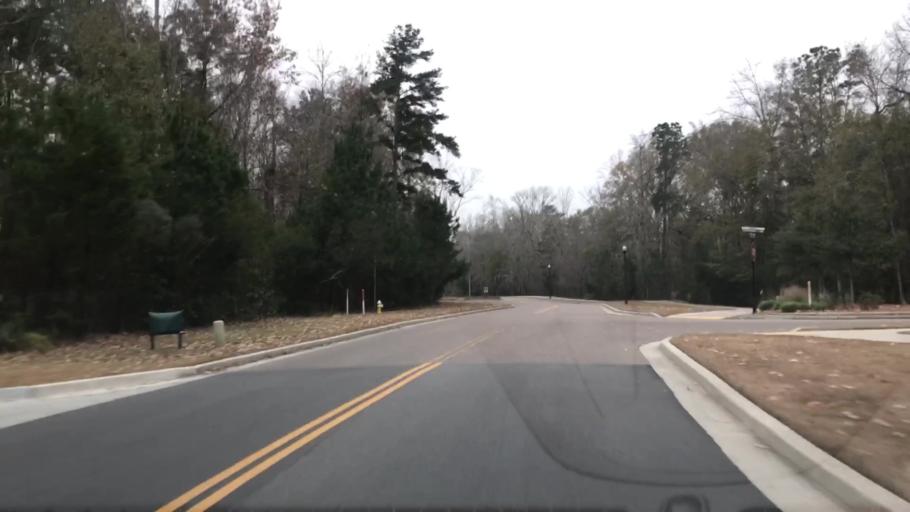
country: US
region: South Carolina
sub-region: Charleston County
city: Shell Point
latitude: 32.8075
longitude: -80.0775
